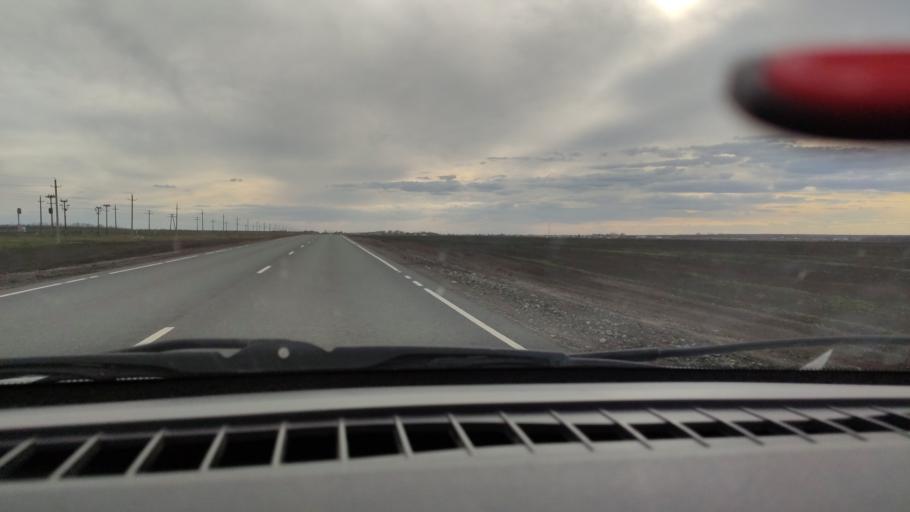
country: RU
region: Bashkortostan
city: Mayachnyy
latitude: 52.3679
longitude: 55.6112
